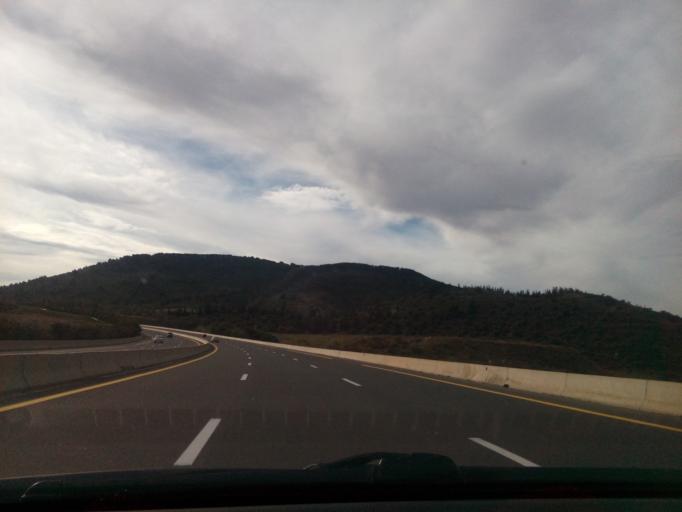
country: DZ
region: Sidi Bel Abbes
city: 'Ain el Berd
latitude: 35.4055
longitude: -0.4923
